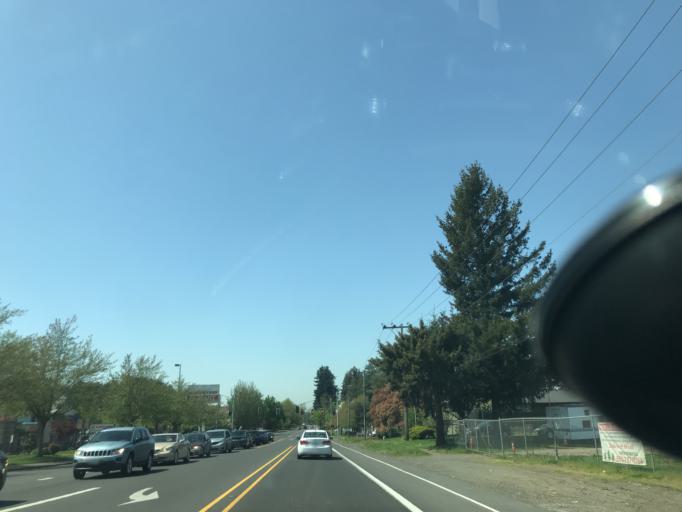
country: US
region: Oregon
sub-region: Multnomah County
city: Gresham
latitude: 45.4924
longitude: -122.4849
